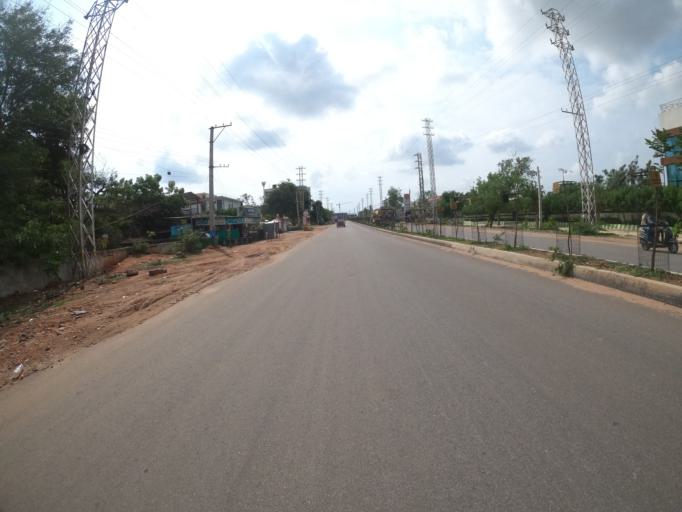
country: IN
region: Telangana
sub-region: Medak
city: Serilingampalle
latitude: 17.3873
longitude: 78.3289
